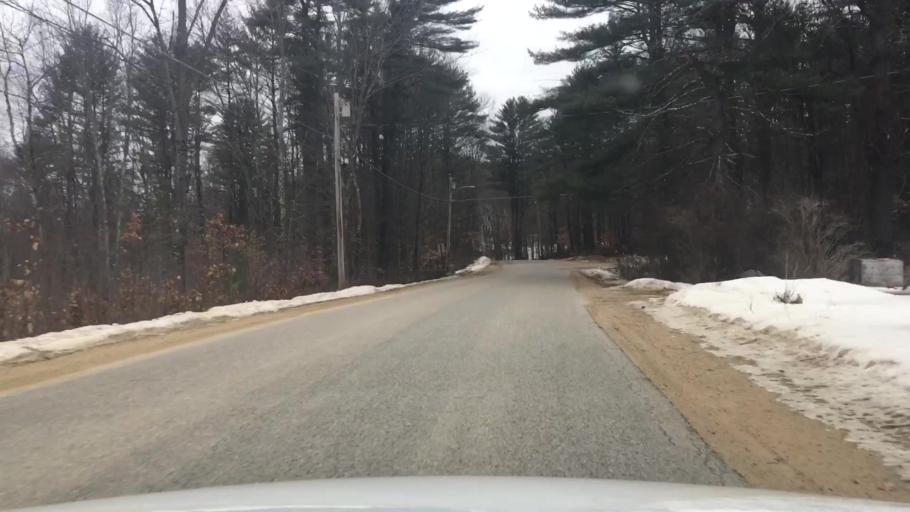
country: US
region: New Hampshire
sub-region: Strafford County
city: Rochester
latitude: 43.3648
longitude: -70.9718
